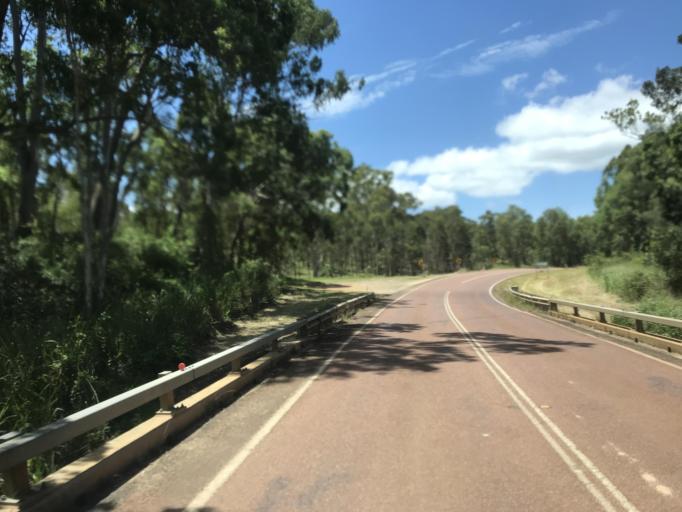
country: AU
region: Queensland
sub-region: Tablelands
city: Ravenshoe
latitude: -17.5953
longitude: 145.4776
